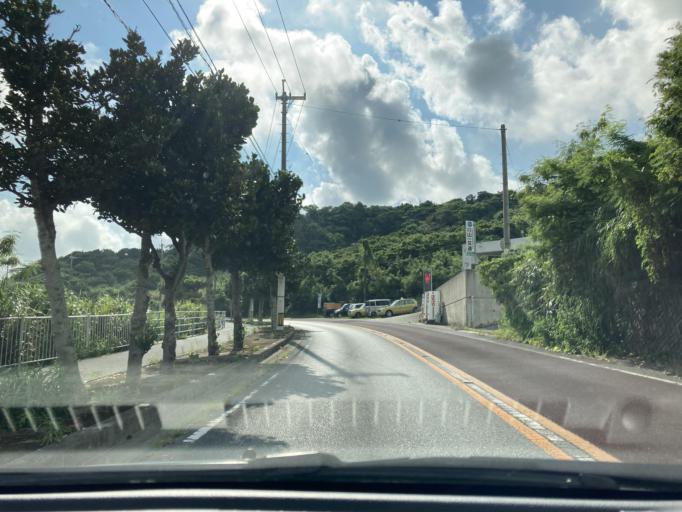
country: JP
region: Okinawa
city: Tomigusuku
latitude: 26.1482
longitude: 127.7567
